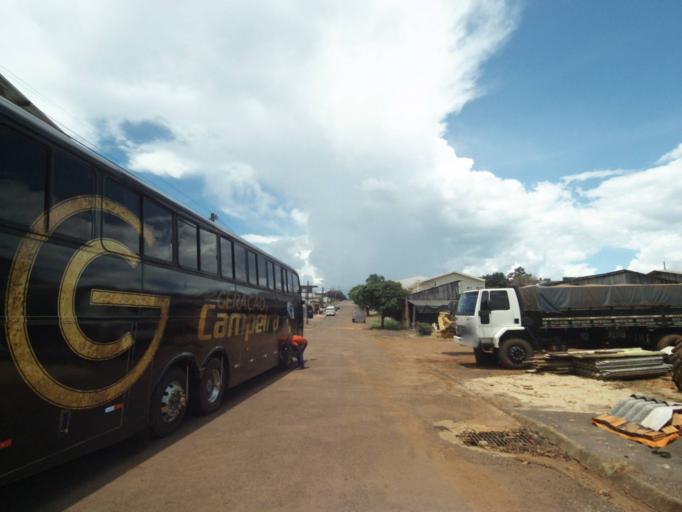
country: BR
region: Parana
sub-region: Guaraniacu
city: Guaraniacu
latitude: -25.0959
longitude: -52.8757
